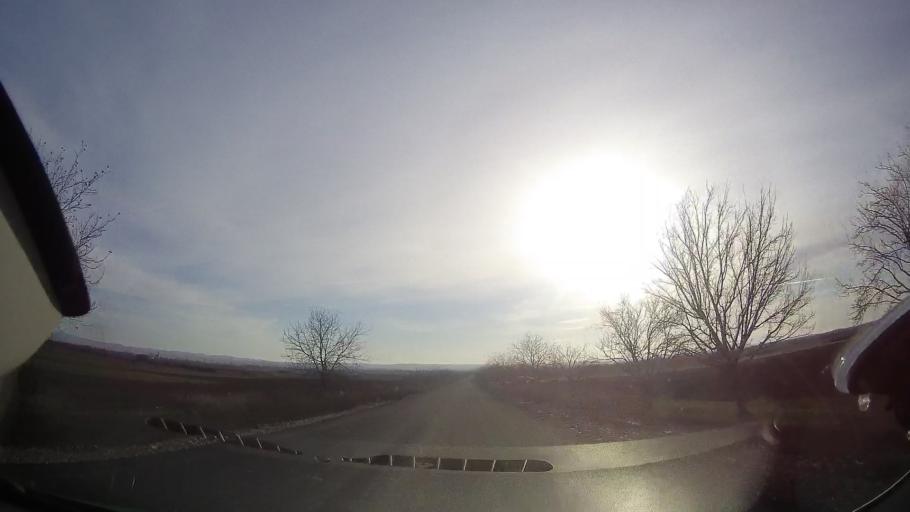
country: RO
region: Bihor
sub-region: Comuna Tileagd
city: Tileagd
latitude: 47.0926
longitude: 22.1783
